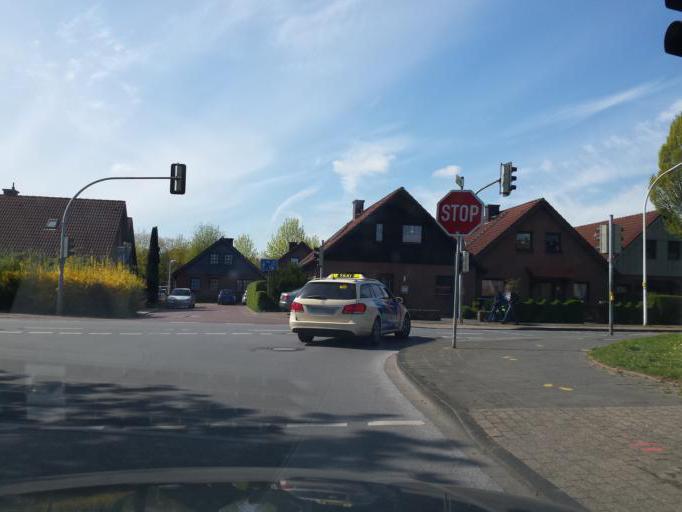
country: DE
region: North Rhine-Westphalia
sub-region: Regierungsbezirk Munster
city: Nottuln
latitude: 51.9252
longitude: 7.3547
